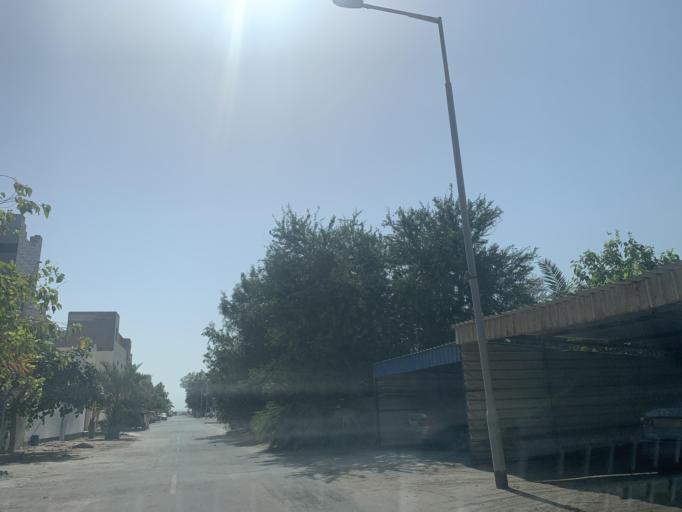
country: BH
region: Manama
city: Jidd Hafs
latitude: 26.2361
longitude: 50.5024
